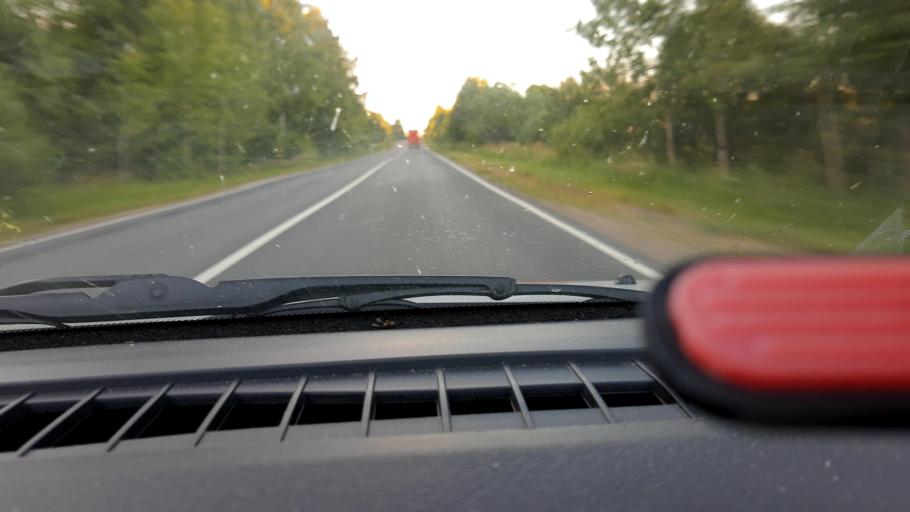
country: RU
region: Nizjnij Novgorod
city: Uren'
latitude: 57.2719
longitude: 45.6279
